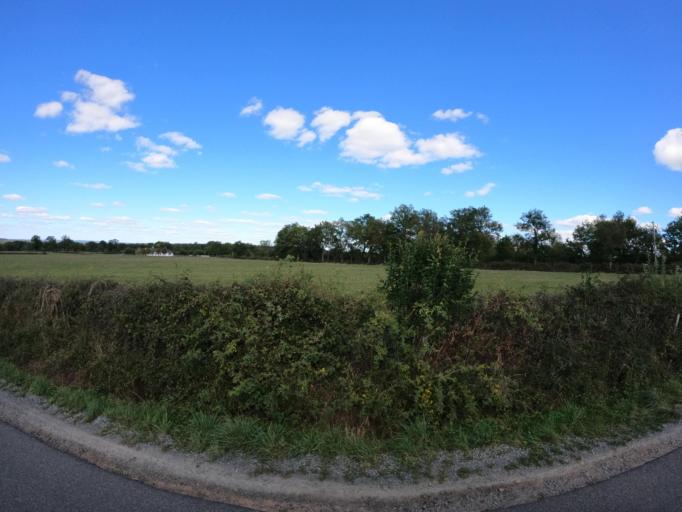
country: FR
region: Auvergne
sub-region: Departement de l'Allier
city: Doyet
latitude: 46.3853
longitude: 2.7722
